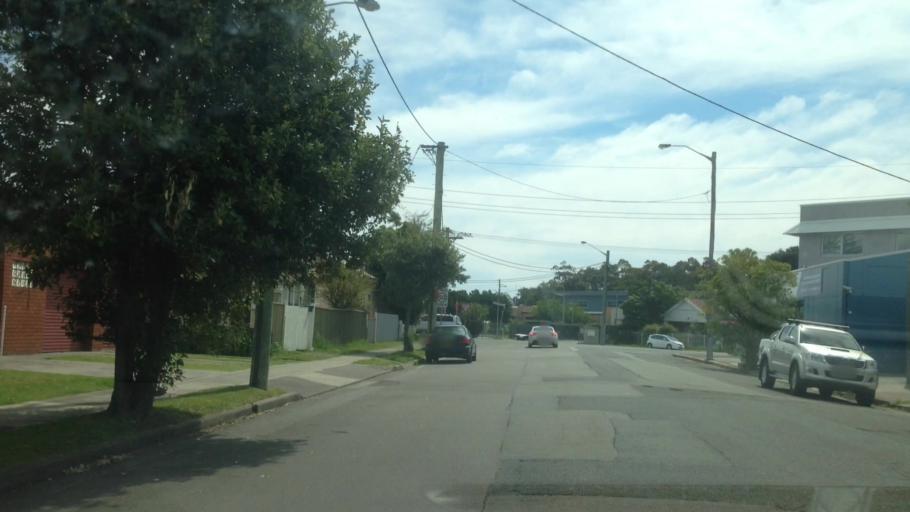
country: AU
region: New South Wales
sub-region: Newcastle
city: Broadmeadow
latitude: -32.9264
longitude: 151.7362
